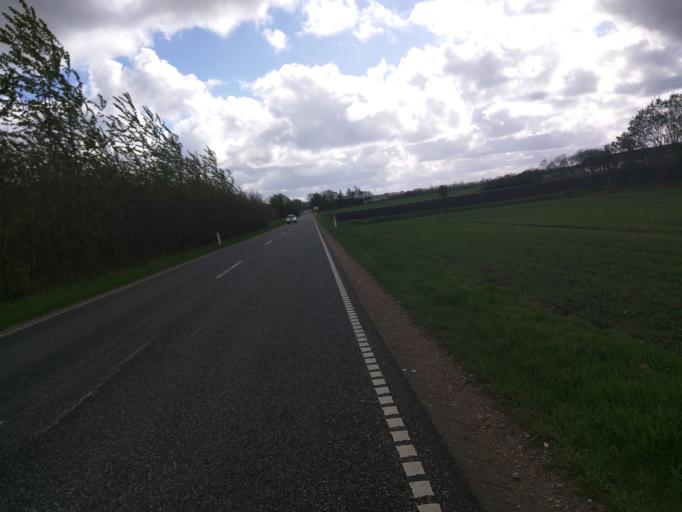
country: DK
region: Central Jutland
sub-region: Viborg Kommune
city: Bjerringbro
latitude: 56.4778
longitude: 9.5598
